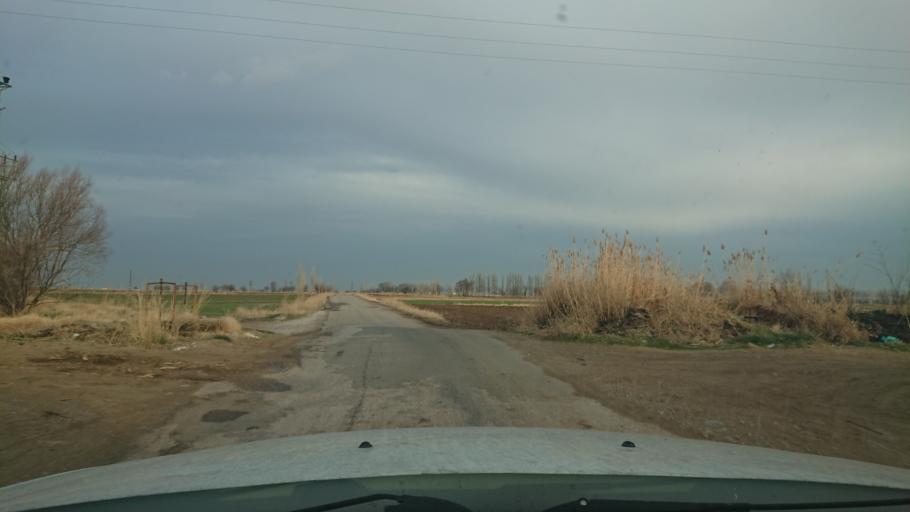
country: TR
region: Aksaray
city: Yesilova
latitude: 38.4392
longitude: 33.8379
